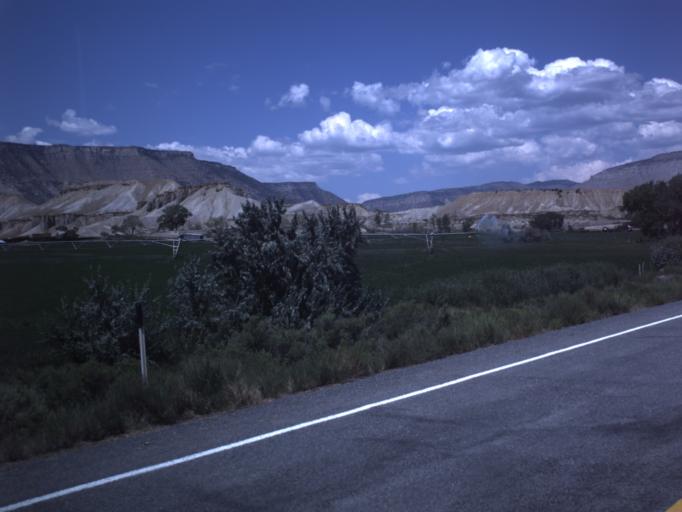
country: US
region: Utah
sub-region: Emery County
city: Orangeville
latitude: 39.2219
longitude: -111.0696
